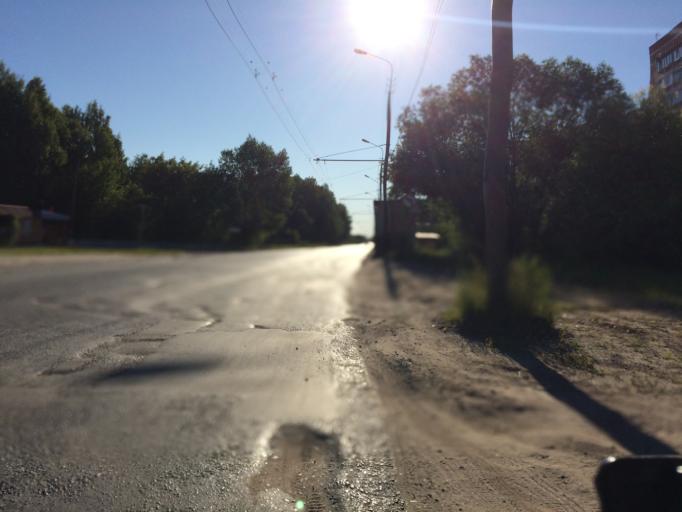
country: RU
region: Mariy-El
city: Yoshkar-Ola
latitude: 56.6522
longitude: 47.8553
